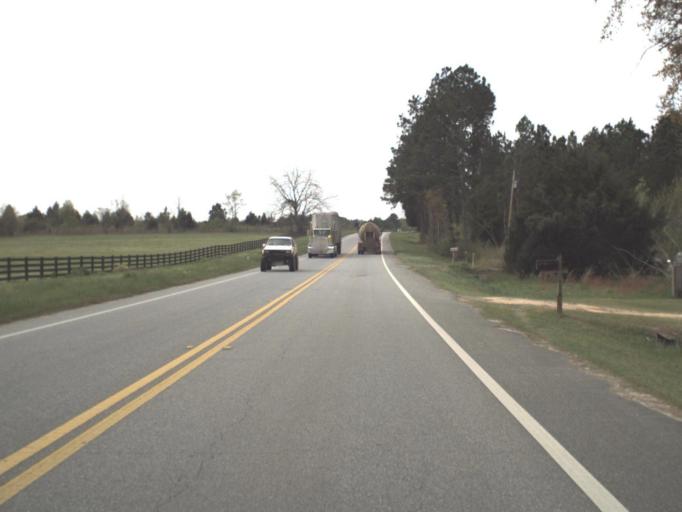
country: US
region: Florida
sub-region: Holmes County
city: Bonifay
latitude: 30.9069
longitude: -85.6512
